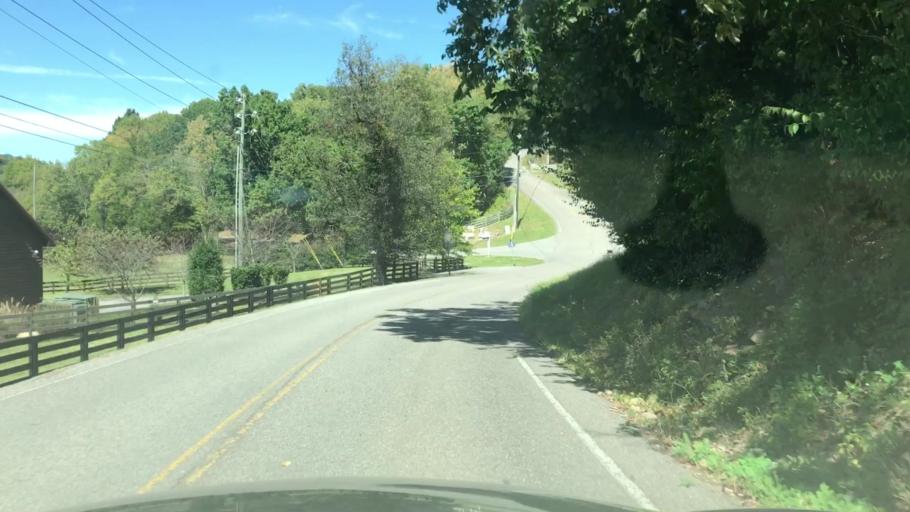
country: US
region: Tennessee
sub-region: Williamson County
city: Franklin
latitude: 35.9924
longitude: -86.8480
